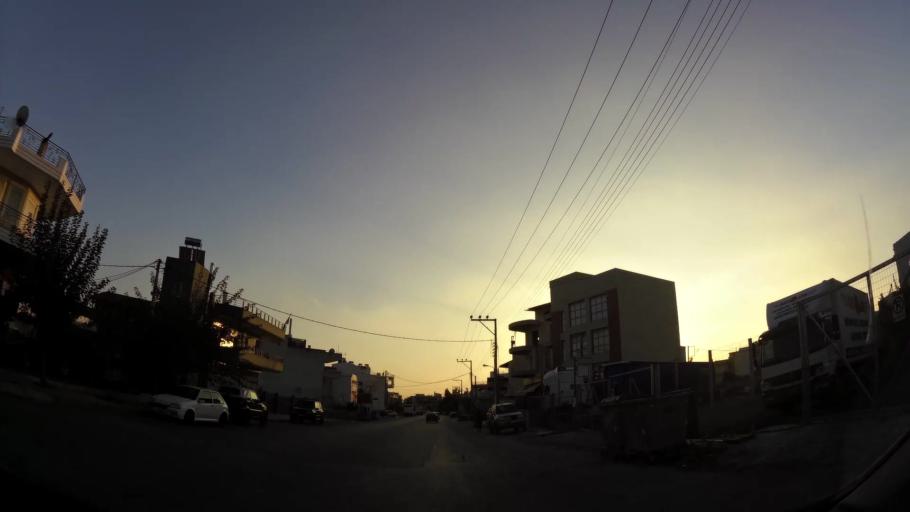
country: GR
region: Attica
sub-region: Nomarchia Anatolikis Attikis
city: Acharnes
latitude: 38.0916
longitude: 23.7457
